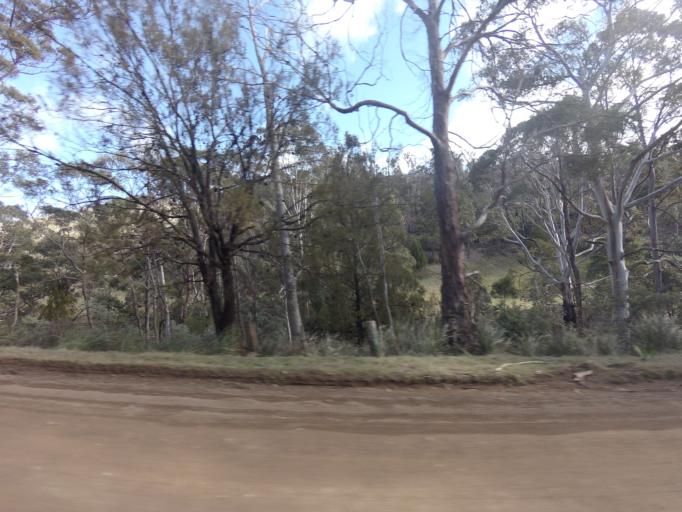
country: AU
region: Tasmania
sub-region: Derwent Valley
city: New Norfolk
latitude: -42.8126
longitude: 147.1305
